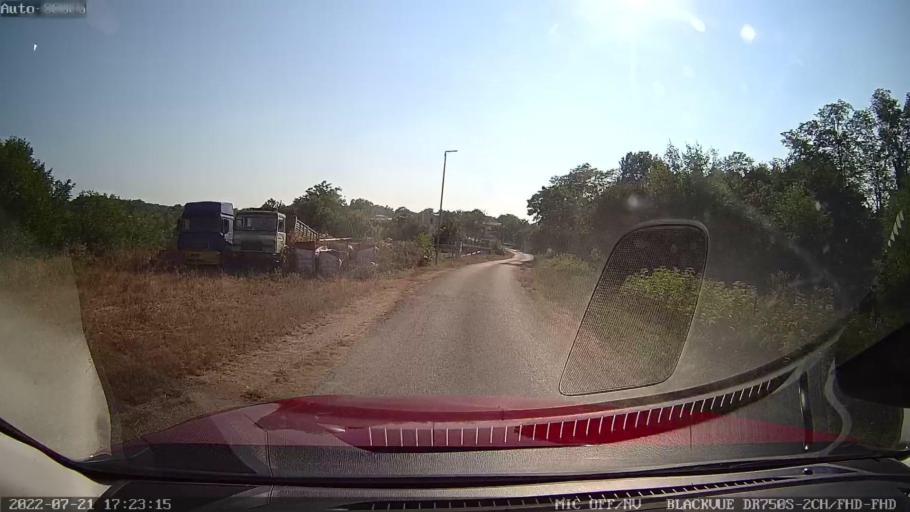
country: HR
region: Istarska
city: Karojba
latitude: 45.1880
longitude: 13.8280
